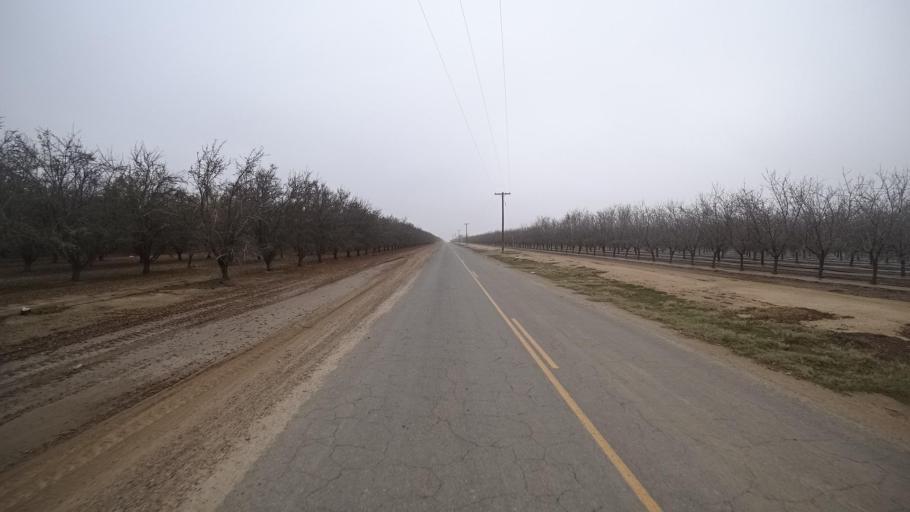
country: US
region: California
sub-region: Kern County
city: Lost Hills
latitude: 35.5864
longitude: -119.5269
